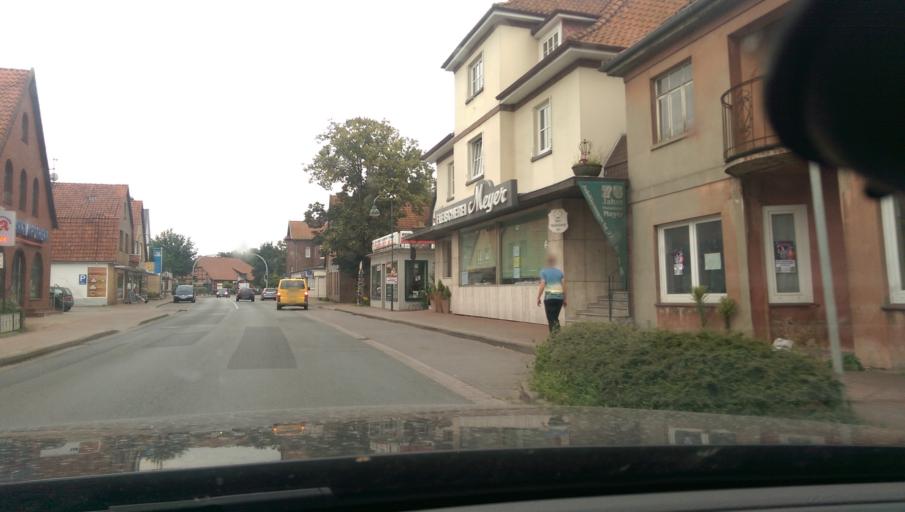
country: DE
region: Lower Saxony
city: Rehburg-Loccum
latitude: 52.4760
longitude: 9.2294
